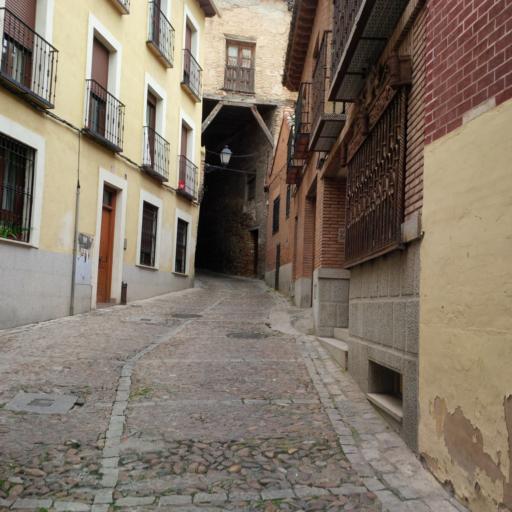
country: ES
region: Castille-La Mancha
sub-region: Province of Toledo
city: Toledo
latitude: 39.8587
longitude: -4.0294
